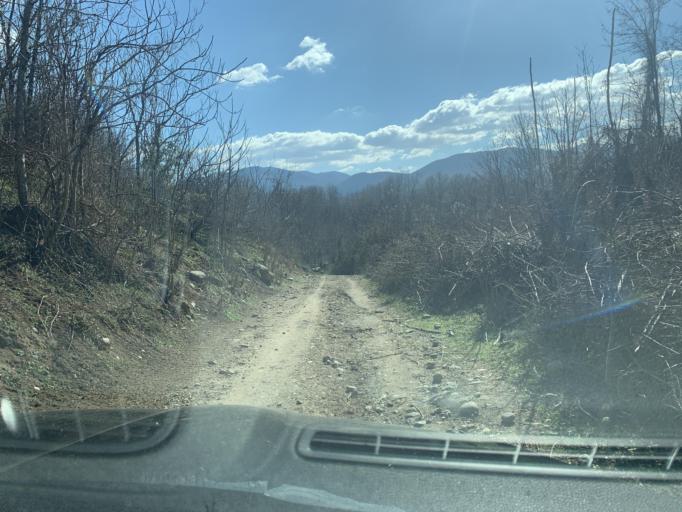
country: MK
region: Demir Kapija
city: Demir Kapija
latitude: 41.3977
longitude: 22.2182
